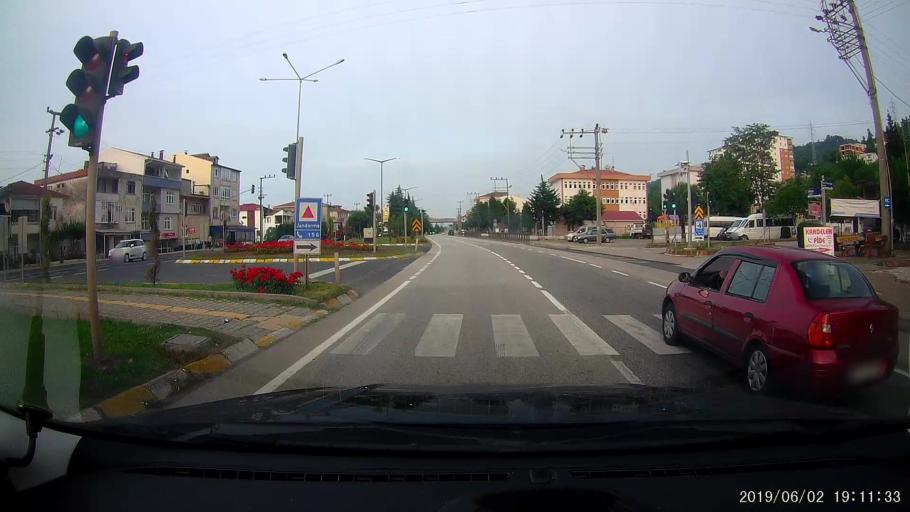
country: TR
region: Ordu
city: Gulyali
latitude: 40.9670
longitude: 38.0560
